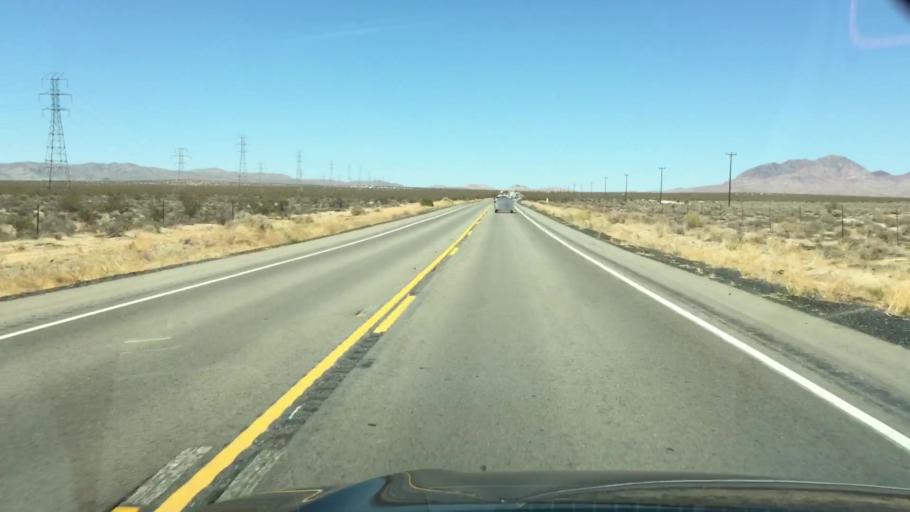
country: US
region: California
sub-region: Kern County
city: Boron
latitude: 35.2406
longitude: -117.6099
